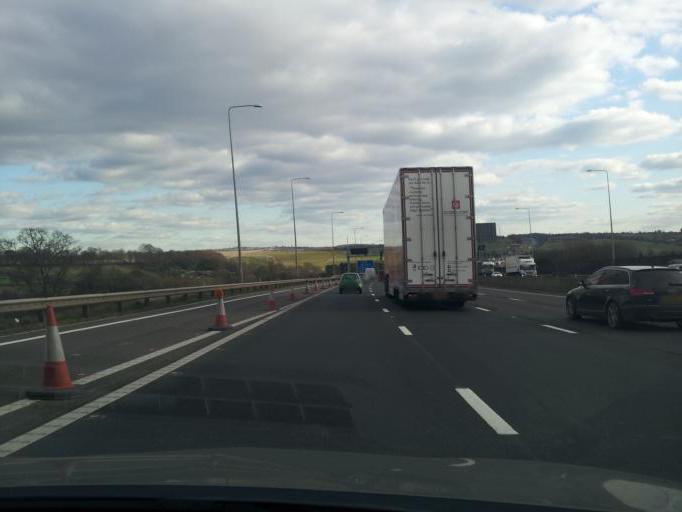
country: GB
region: England
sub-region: Derbyshire
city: Pinxton
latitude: 53.0967
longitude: -1.3132
